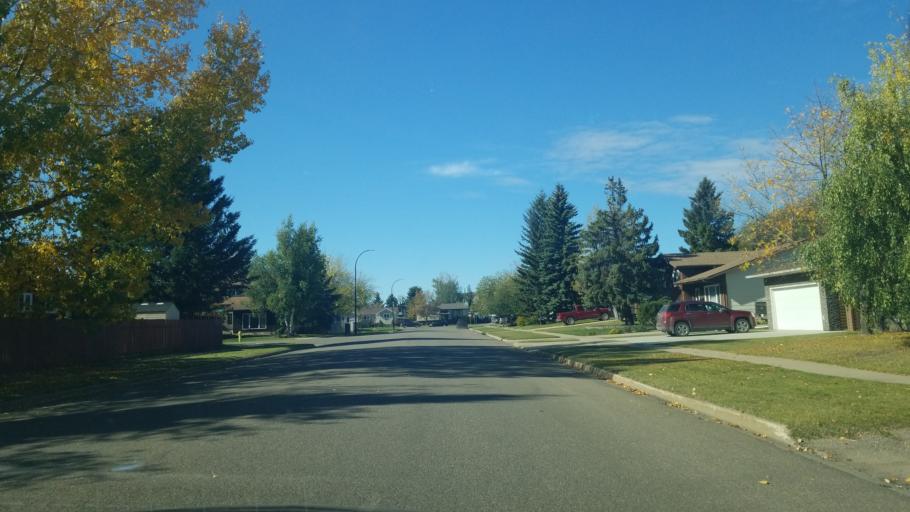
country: CA
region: Saskatchewan
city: Lloydminster
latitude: 53.2729
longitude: -110.0221
